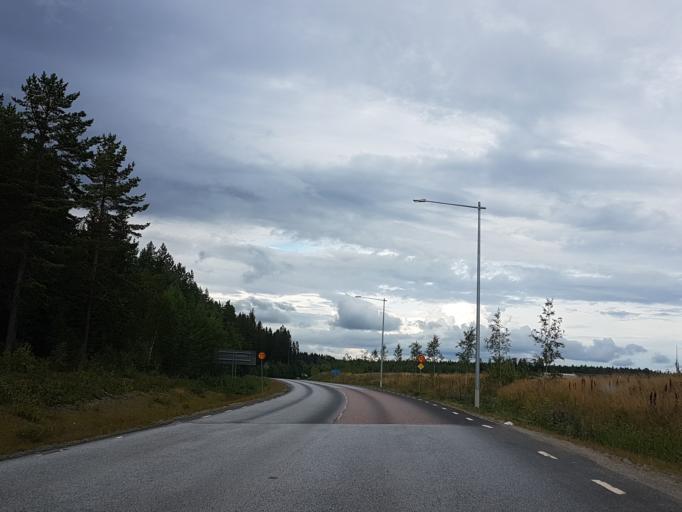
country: SE
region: Vaesterbotten
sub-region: Umea Kommun
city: Ersmark
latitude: 63.8041
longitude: 20.3639
